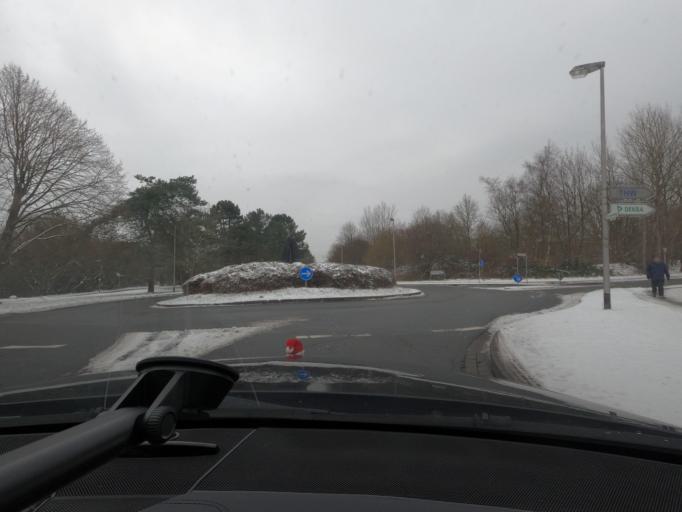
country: DE
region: Schleswig-Holstein
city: Jarplund-Weding
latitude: 54.7645
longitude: 9.3949
